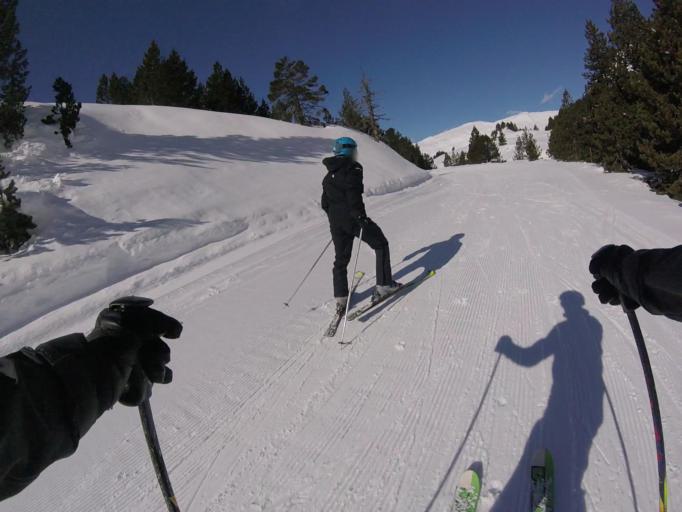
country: ES
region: Catalonia
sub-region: Provincia de Lleida
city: Vielha
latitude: 42.7029
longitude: 0.9654
